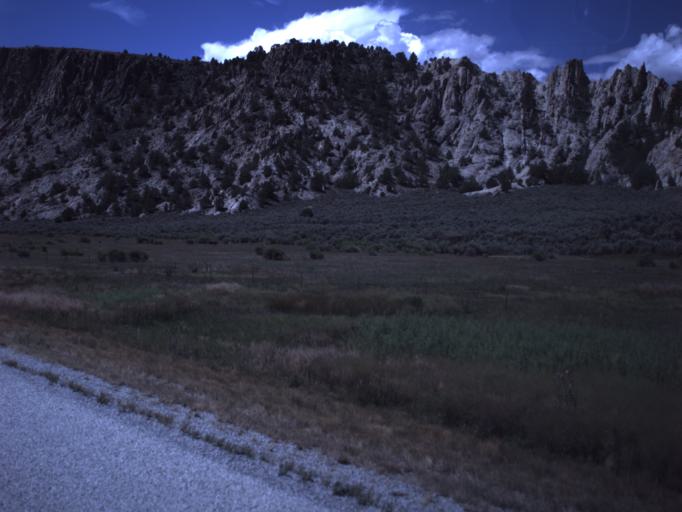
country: US
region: Utah
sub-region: Garfield County
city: Panguitch
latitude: 38.0345
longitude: -112.3565
